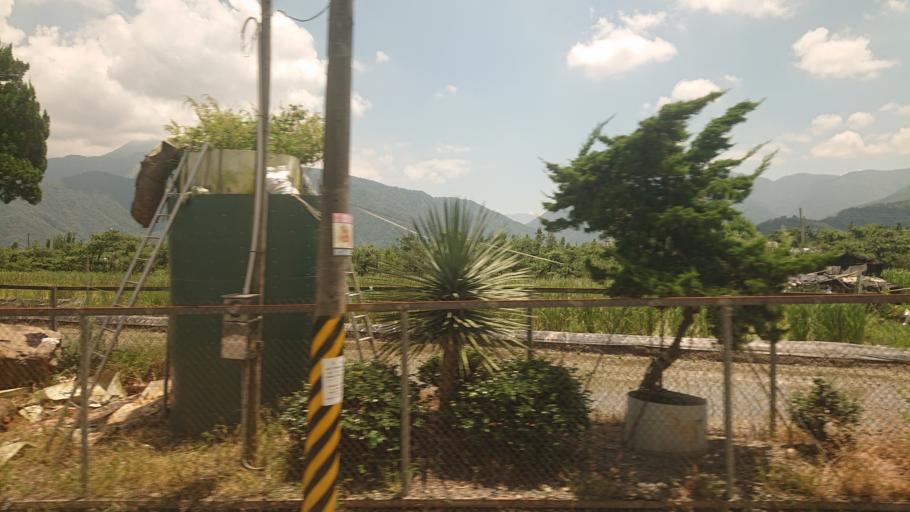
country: TW
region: Taiwan
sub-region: Nantou
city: Puli
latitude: 23.9769
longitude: 120.9618
